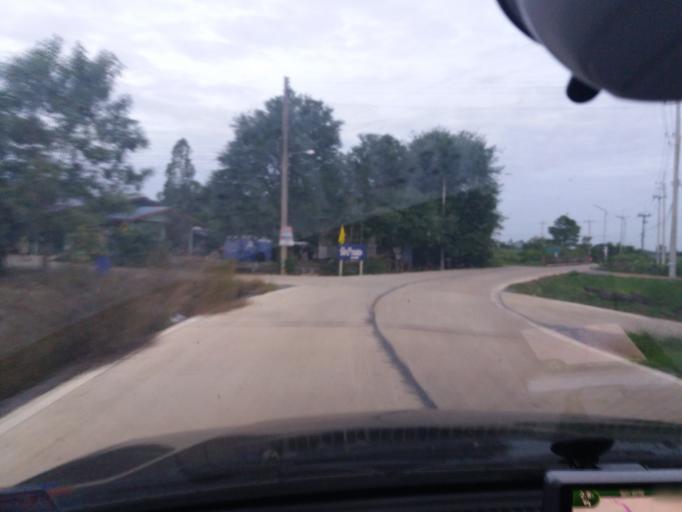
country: TH
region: Suphan Buri
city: Ban Sam Chuk
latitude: 14.7311
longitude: 100.0820
